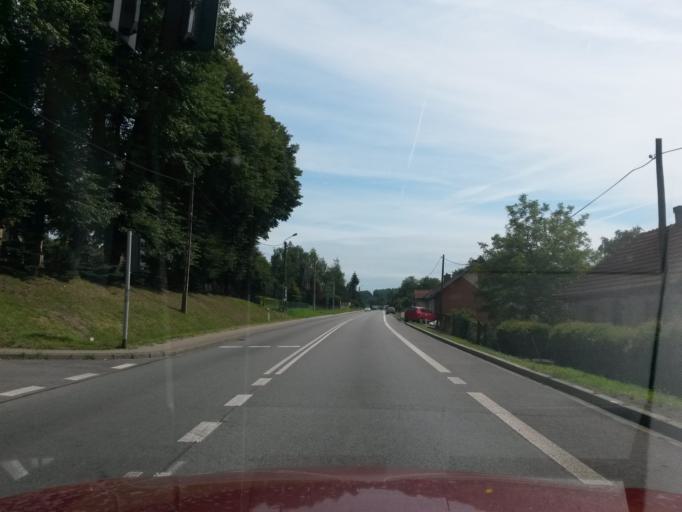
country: PL
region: Lesser Poland Voivodeship
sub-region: Powiat bochenski
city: Lapczyca
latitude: 49.9604
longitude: 20.3750
